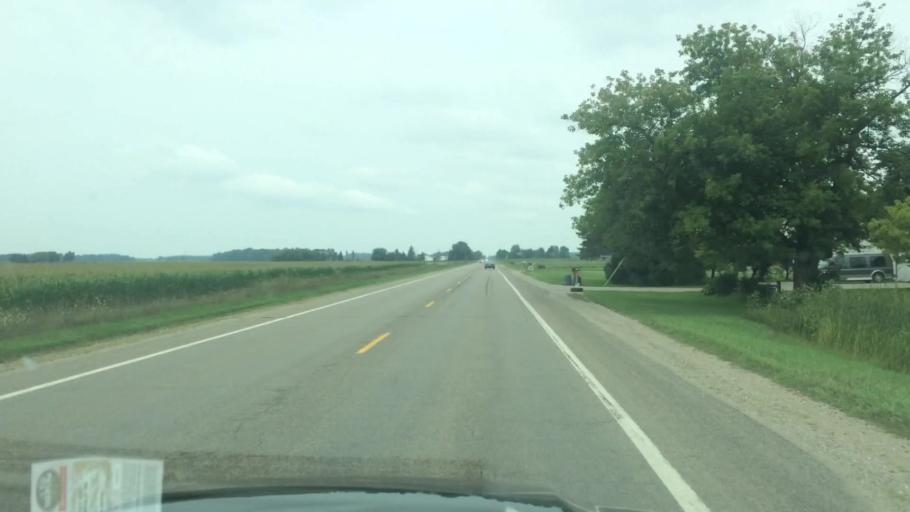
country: US
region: Michigan
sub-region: Huron County
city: Bad Axe
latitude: 43.8428
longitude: -83.0016
